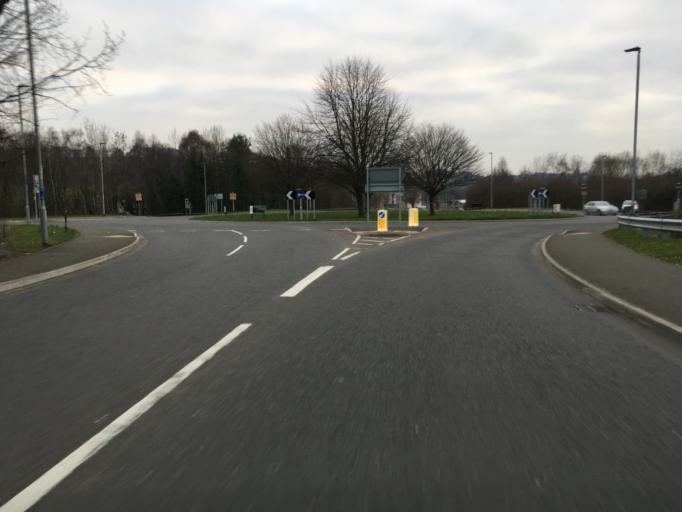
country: GB
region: Wales
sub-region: Caerphilly County Borough
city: Risca
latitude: 51.5862
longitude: -3.0519
